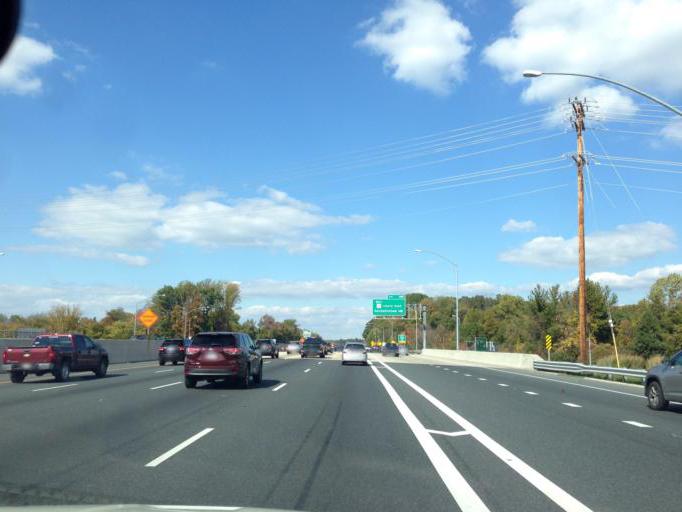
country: US
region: Maryland
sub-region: Baltimore County
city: Lochearn
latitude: 39.3482
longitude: -76.7452
